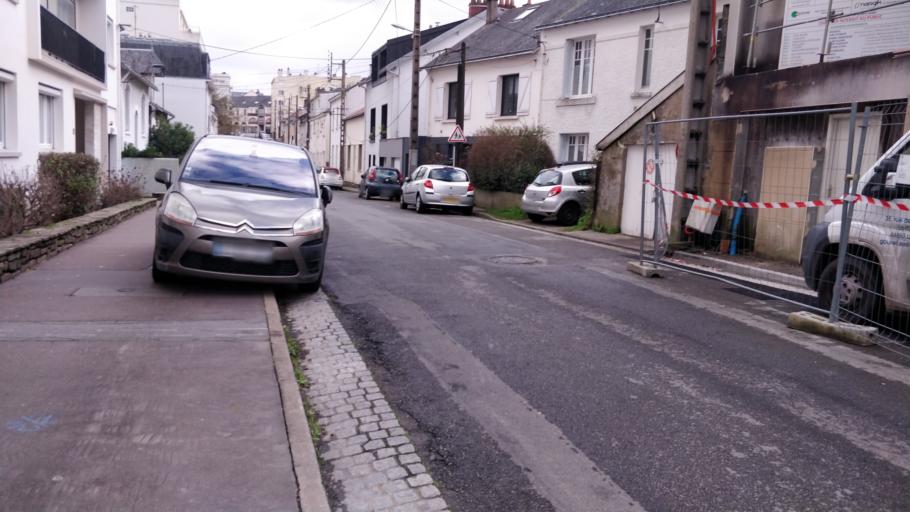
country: FR
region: Pays de la Loire
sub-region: Departement de la Loire-Atlantique
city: Nantes
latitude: 47.2342
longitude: -1.5451
